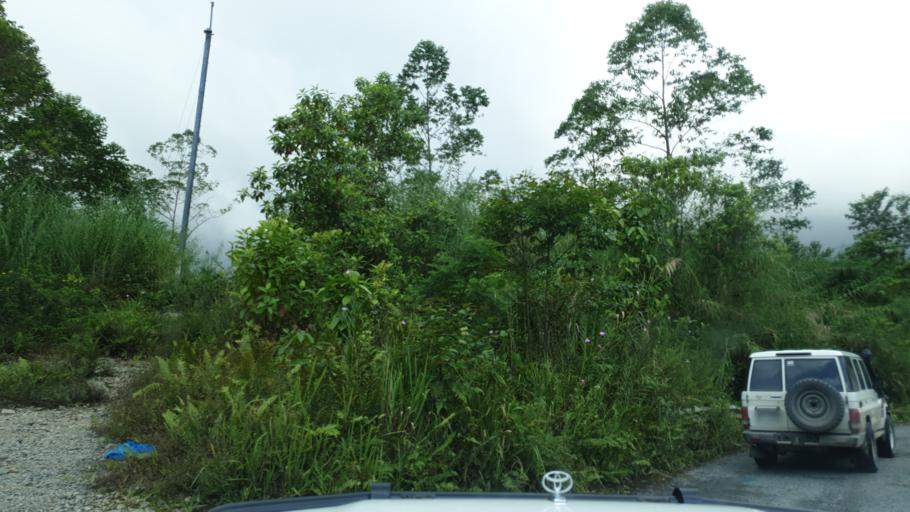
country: PG
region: Bougainville
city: Panguna
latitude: -6.3075
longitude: 155.4884
